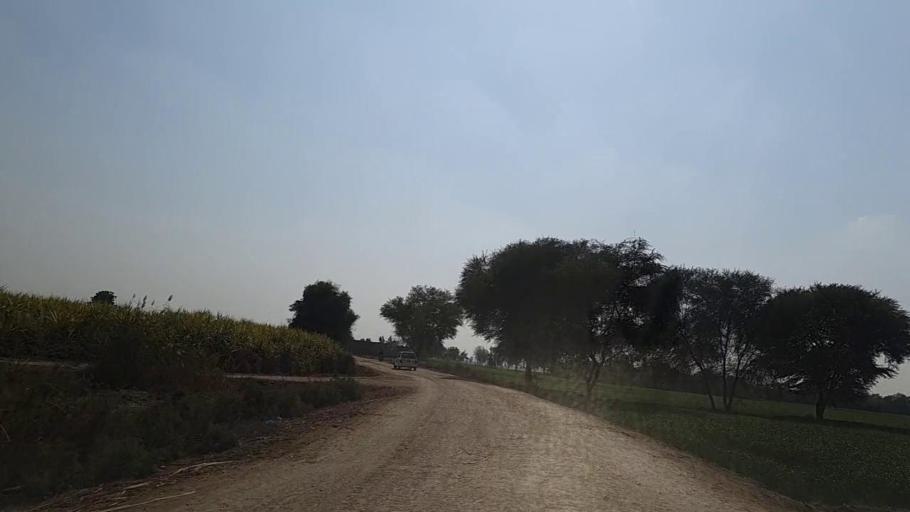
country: PK
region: Sindh
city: Daur
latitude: 26.4691
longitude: 68.2506
